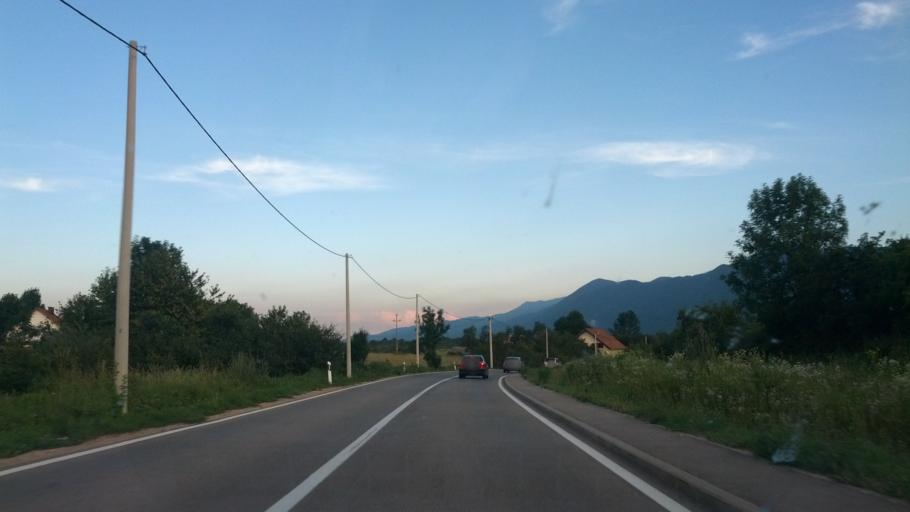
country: BA
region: Federation of Bosnia and Herzegovina
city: Izacic
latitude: 44.9032
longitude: 15.7234
